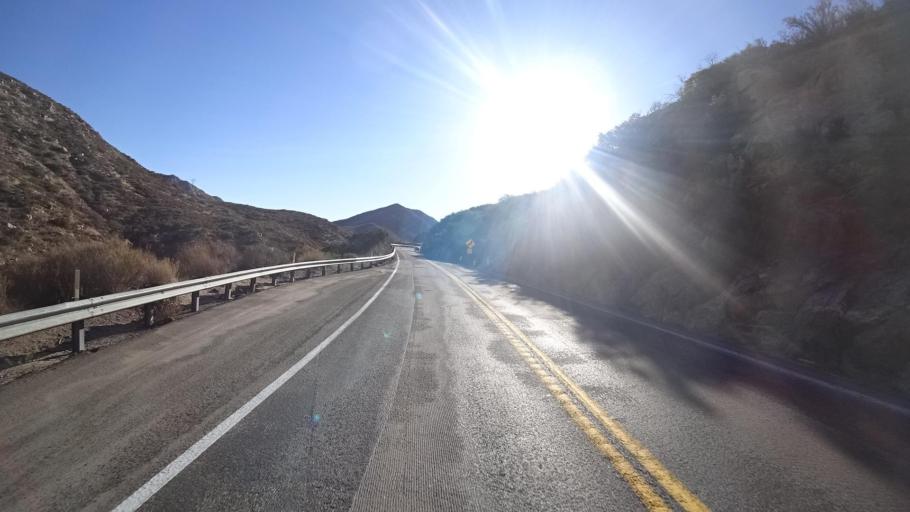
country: MX
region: Baja California
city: Tecate
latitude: 32.5950
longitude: -116.6721
